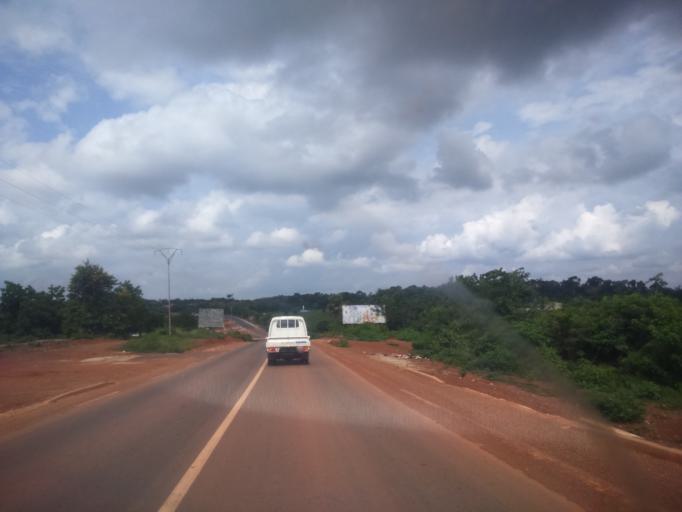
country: CI
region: Moyen-Comoe
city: Abengourou
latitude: 6.7212
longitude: -3.5262
